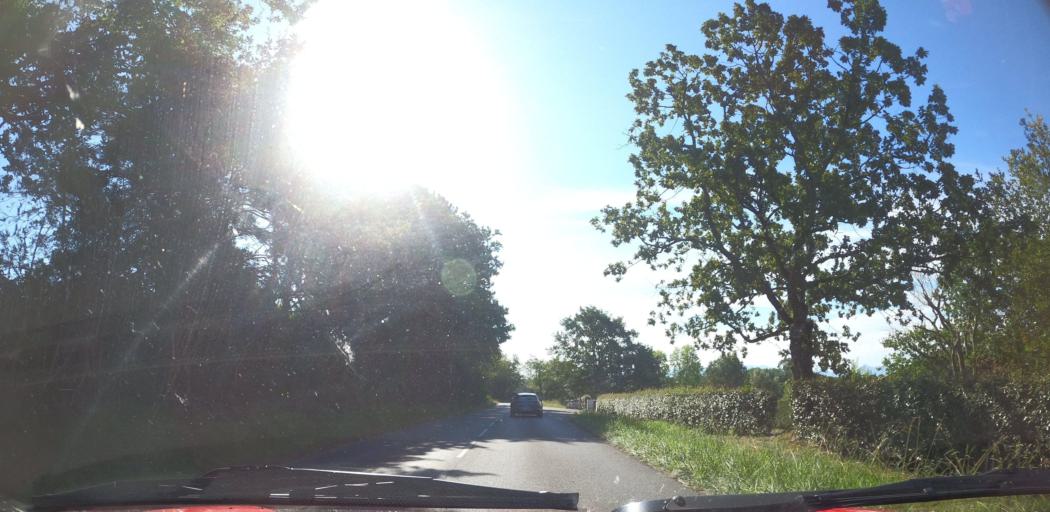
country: FR
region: Aquitaine
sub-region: Departement des Pyrenees-Atlantiques
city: Arbonne
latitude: 43.4055
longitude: -1.5383
